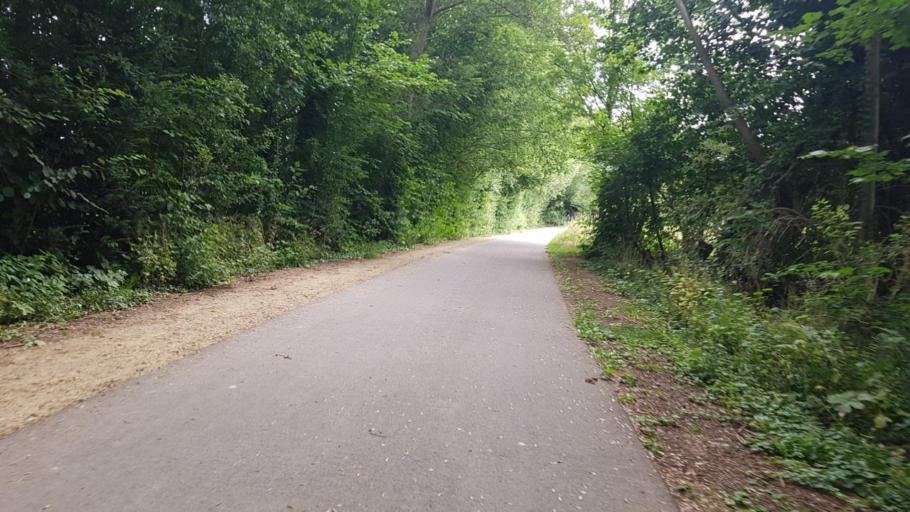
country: BE
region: Wallonia
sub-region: Province de Liege
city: Plombieres
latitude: 50.7459
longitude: 5.9768
